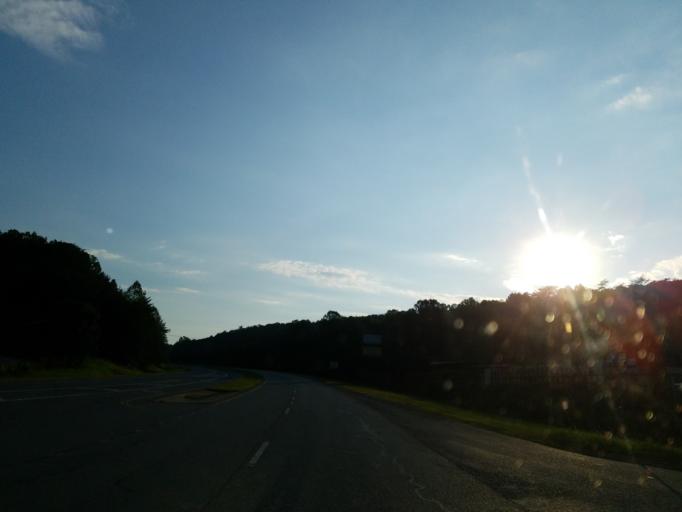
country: US
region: Georgia
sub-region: Gilmer County
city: Ellijay
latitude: 34.7212
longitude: -84.4468
